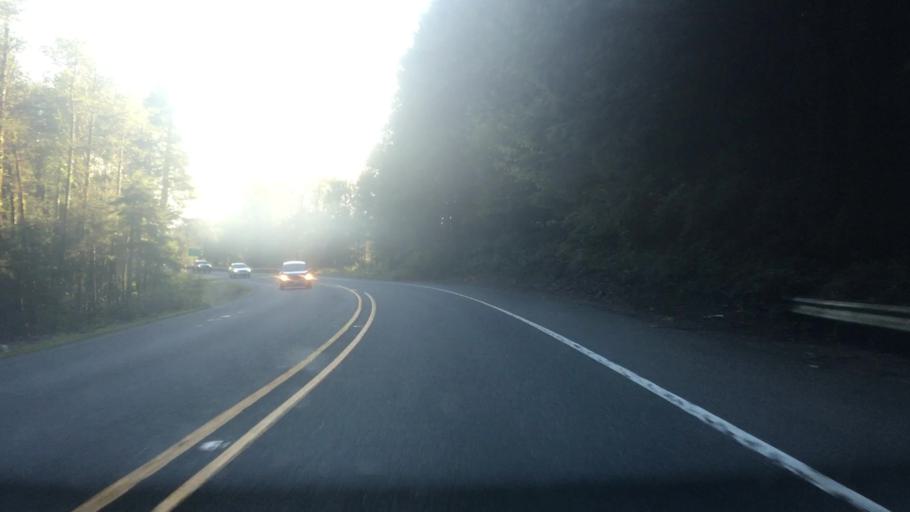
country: US
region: Oregon
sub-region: Clatsop County
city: Cannon Beach
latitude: 45.9127
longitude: -123.9478
